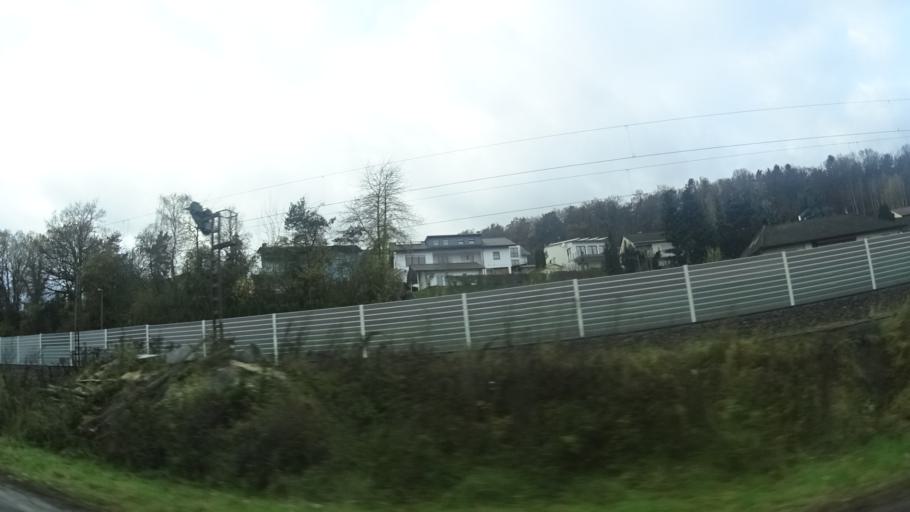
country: DE
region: Hesse
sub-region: Regierungsbezirk Kassel
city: Petersberg
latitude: 50.5856
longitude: 9.7309
